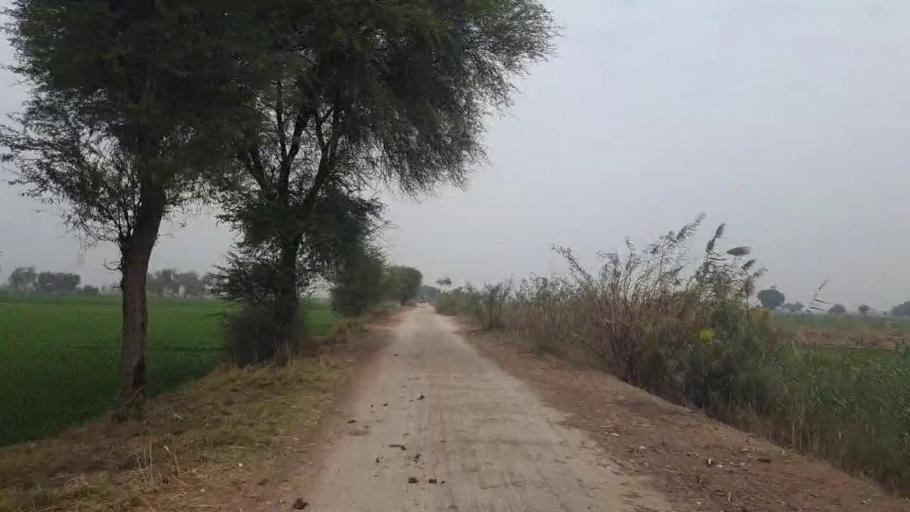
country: PK
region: Sindh
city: Tando Adam
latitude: 25.7261
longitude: 68.7386
